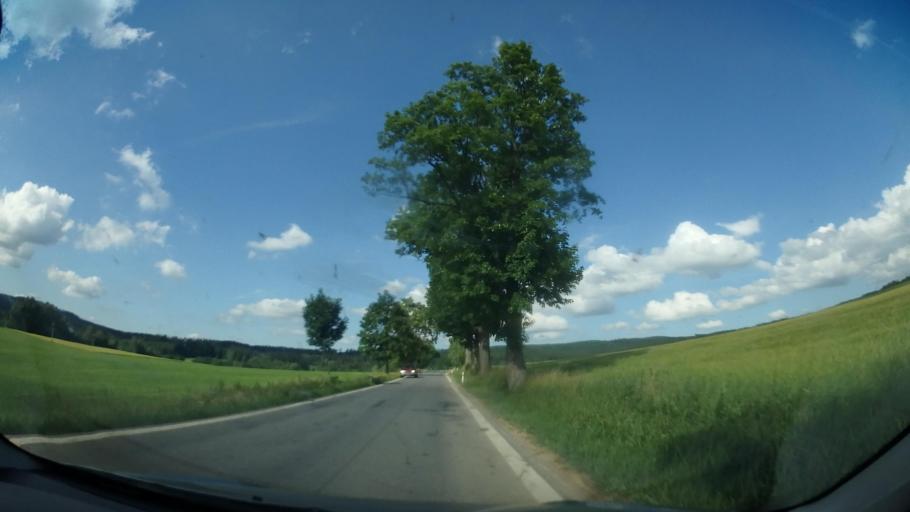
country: CZ
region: Vysocina
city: Zd'ar nad Sazavou Druhy
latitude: 49.6255
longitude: 15.9593
